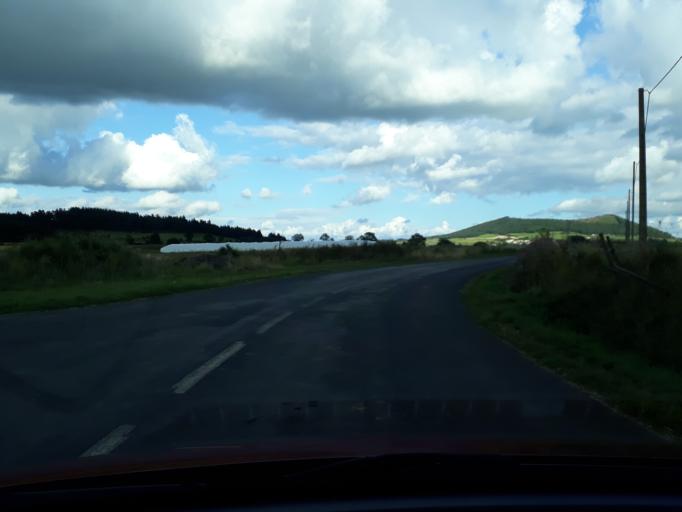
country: FR
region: Languedoc-Roussillon
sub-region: Departement de la Lozere
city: Langogne
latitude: 44.8227
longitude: 3.9242
